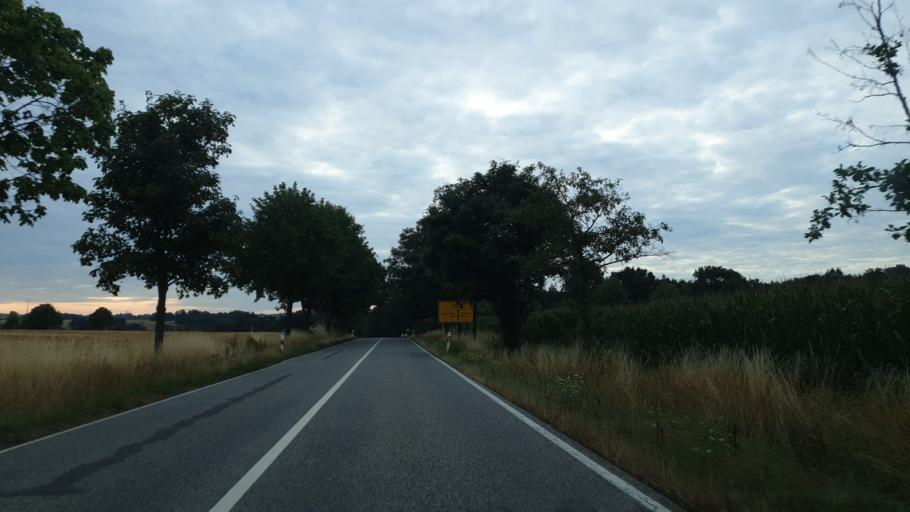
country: DE
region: Saxony
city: Callenberg
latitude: 50.8449
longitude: 12.6694
